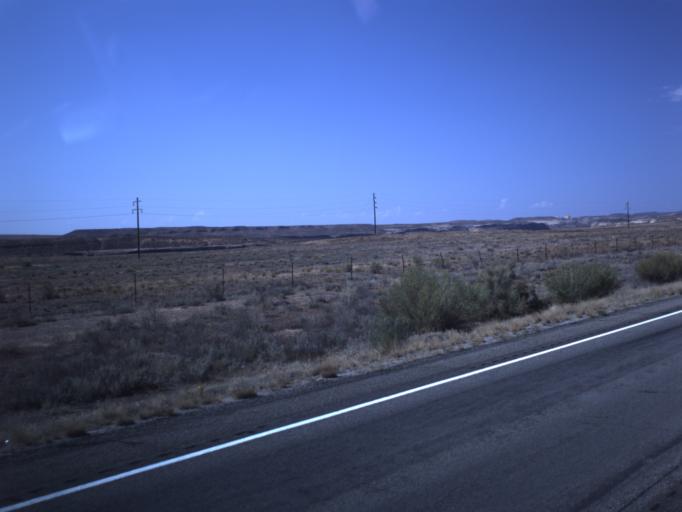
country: US
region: Utah
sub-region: San Juan County
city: Blanding
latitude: 37.2683
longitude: -109.6045
